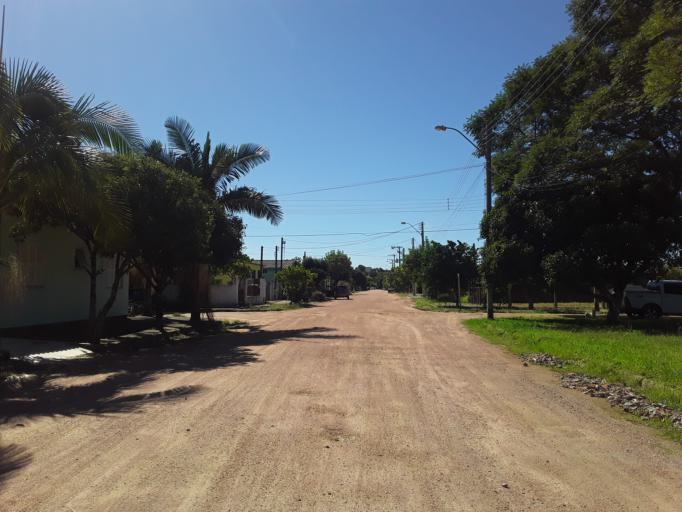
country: BR
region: Rio Grande do Sul
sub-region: Sao Lourenco Do Sul
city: Sao Lourenco do Sul
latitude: -31.3478
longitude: -51.9918
